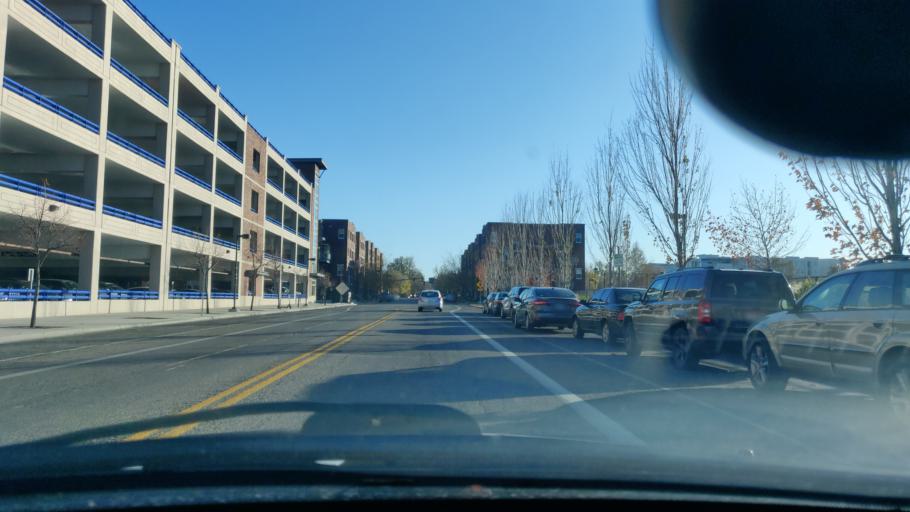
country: US
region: Idaho
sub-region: Ada County
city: Boise
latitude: 43.6007
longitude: -116.2024
